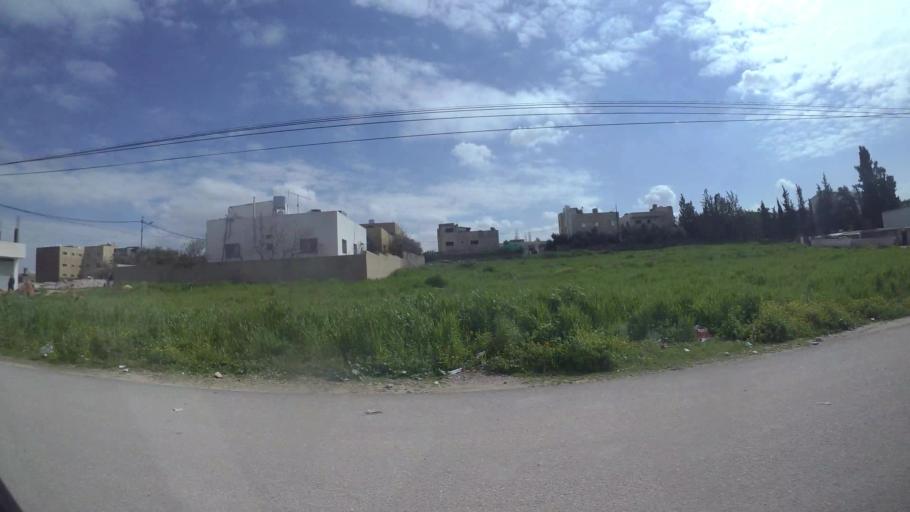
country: JO
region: Amman
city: Al Jubayhah
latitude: 32.0620
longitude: 35.8226
